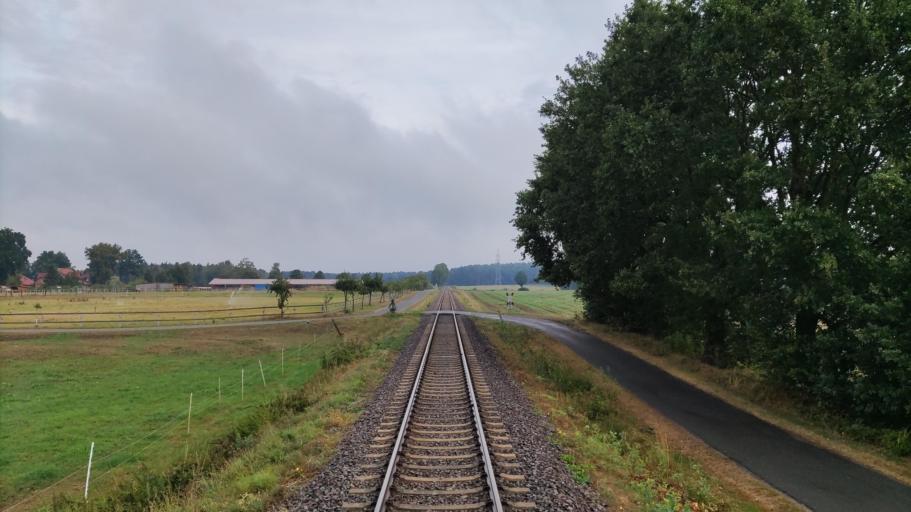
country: DE
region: Lower Saxony
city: Soltau
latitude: 52.9940
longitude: 9.8865
